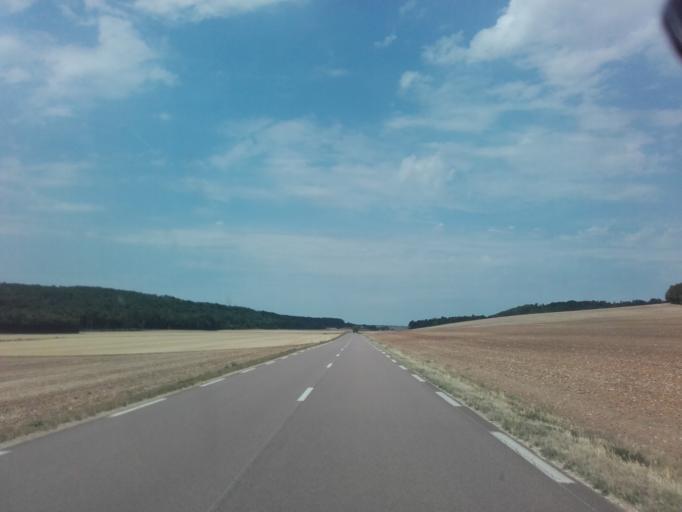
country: FR
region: Bourgogne
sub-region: Departement de l'Yonne
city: Chablis
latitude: 47.7662
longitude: 3.8165
